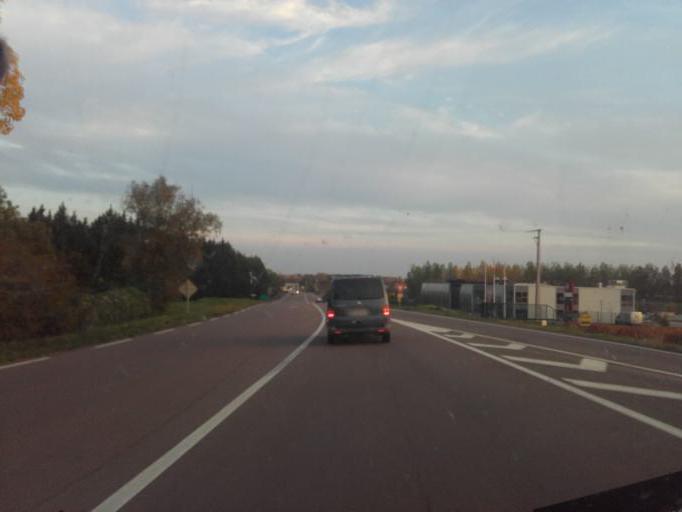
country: FR
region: Bourgogne
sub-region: Departement de la Cote-d'Or
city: Corpeau
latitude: 46.9250
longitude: 4.7440
